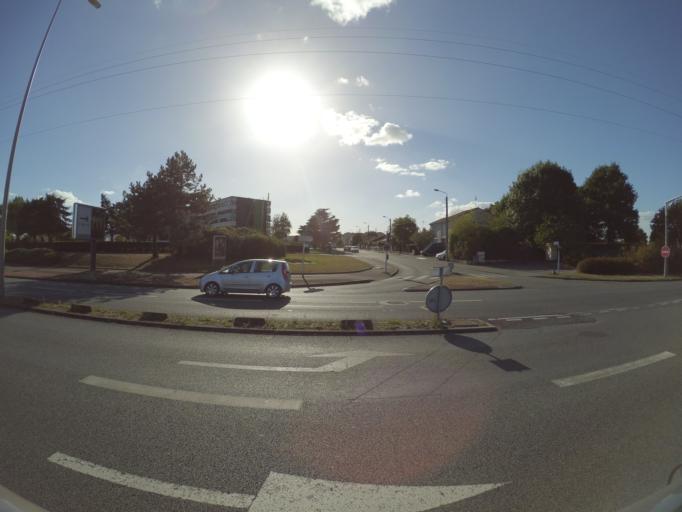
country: FR
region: Pays de la Loire
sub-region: Departement de Maine-et-Loire
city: Cholet
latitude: 47.0469
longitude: -0.8964
